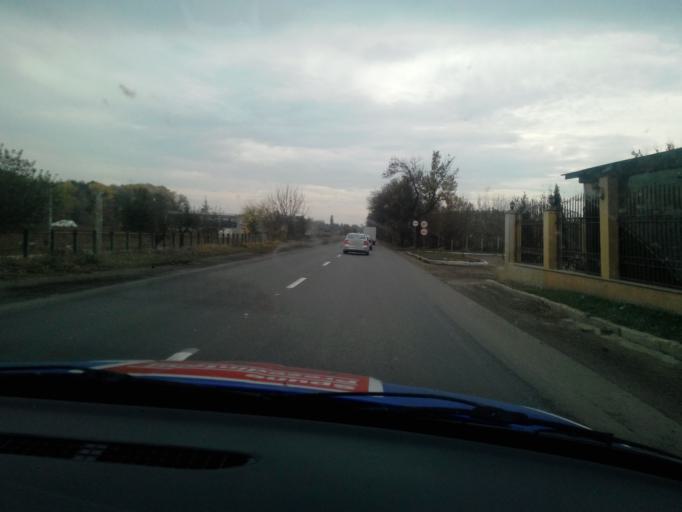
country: RO
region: Vaslui
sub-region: Municipiul Barlad
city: Barlad
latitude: 46.2587
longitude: 27.6850
